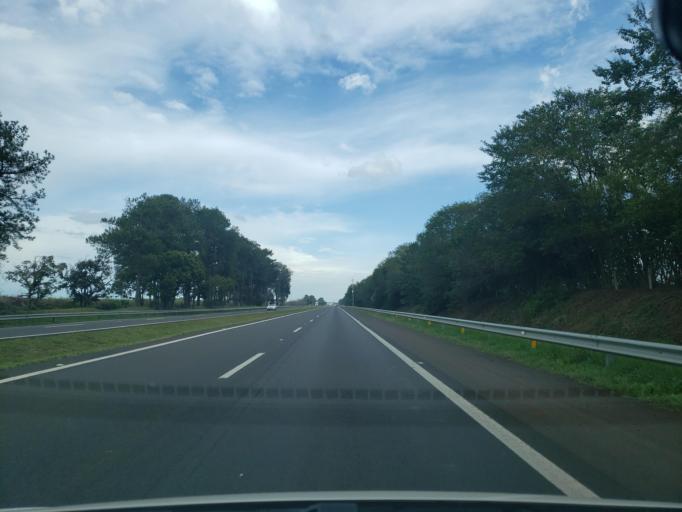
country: BR
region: Sao Paulo
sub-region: Itirapina
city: Itirapina
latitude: -22.2657
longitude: -47.9183
